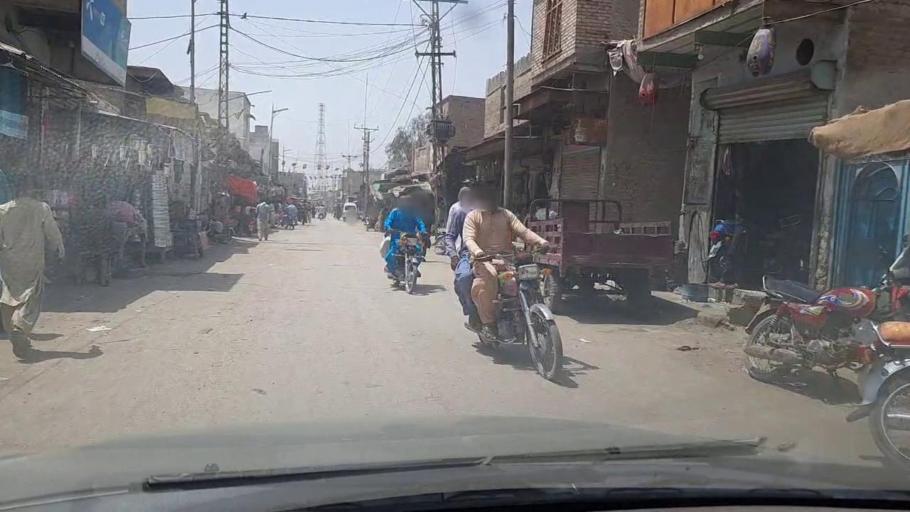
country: PK
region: Sindh
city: Miro Khan
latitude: 27.7614
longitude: 68.0935
